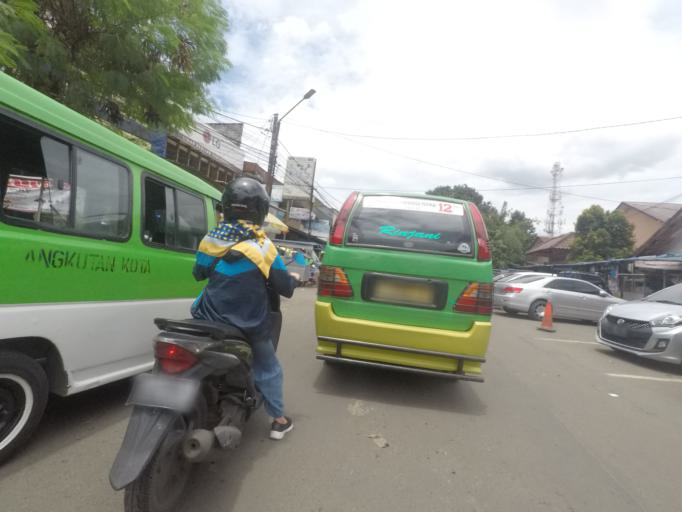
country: ID
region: West Java
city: Bogor
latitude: -6.5920
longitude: 106.7929
